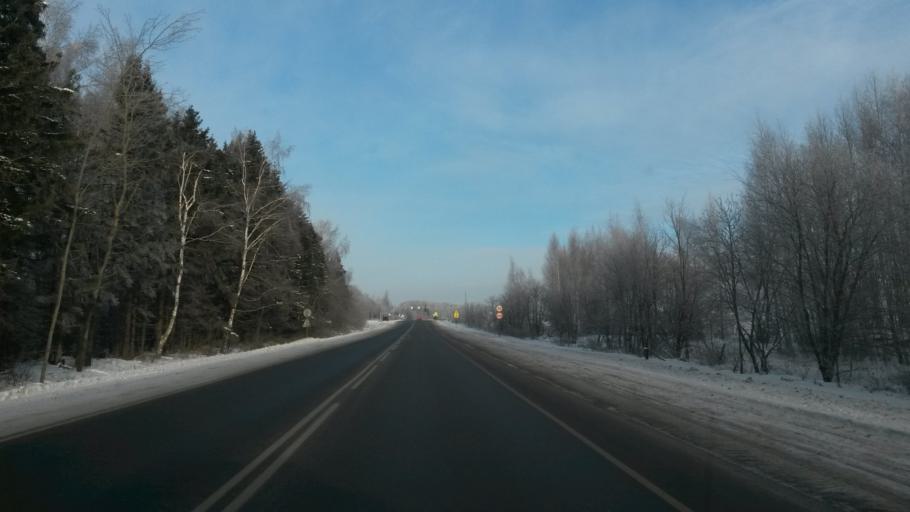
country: RU
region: Vladimir
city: Bogolyubovo
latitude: 56.2176
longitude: 40.4411
